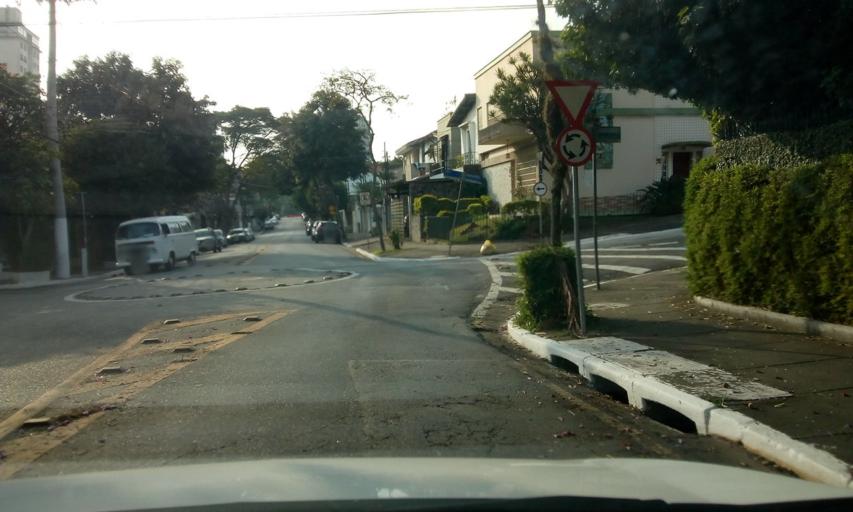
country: BR
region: Sao Paulo
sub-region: Sao Paulo
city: Sao Paulo
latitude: -23.6136
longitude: -46.6527
